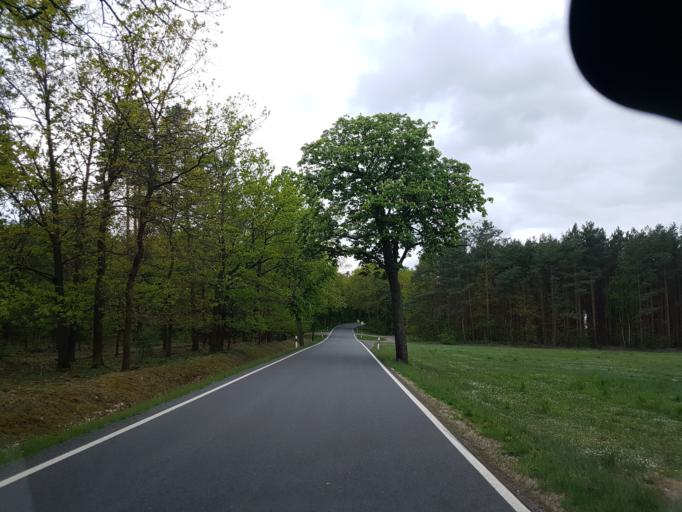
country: DE
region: Brandenburg
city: Bronkow
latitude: 51.6334
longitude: 13.9456
